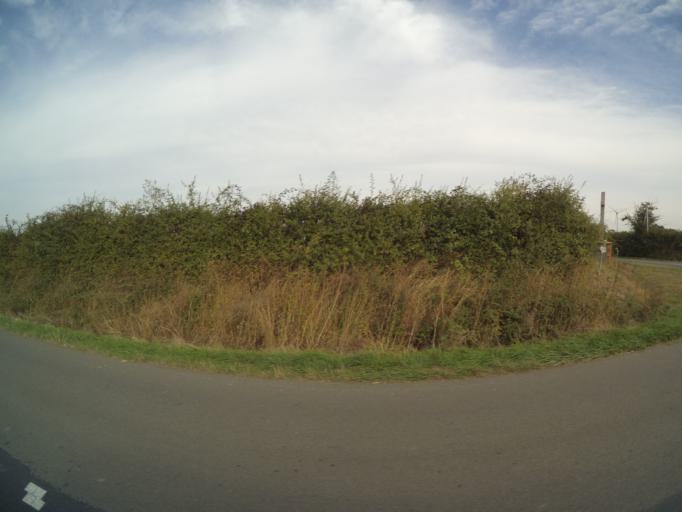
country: FR
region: Pays de la Loire
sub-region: Departement de Maine-et-Loire
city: Vihiers
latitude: 47.2059
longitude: -0.5692
